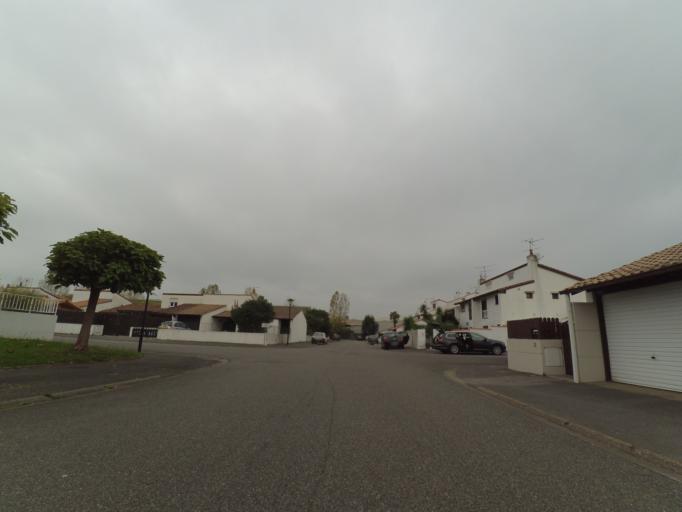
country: ES
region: Basque Country
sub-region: Provincia de Guipuzcoa
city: Irun
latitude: 43.3447
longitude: -1.7686
